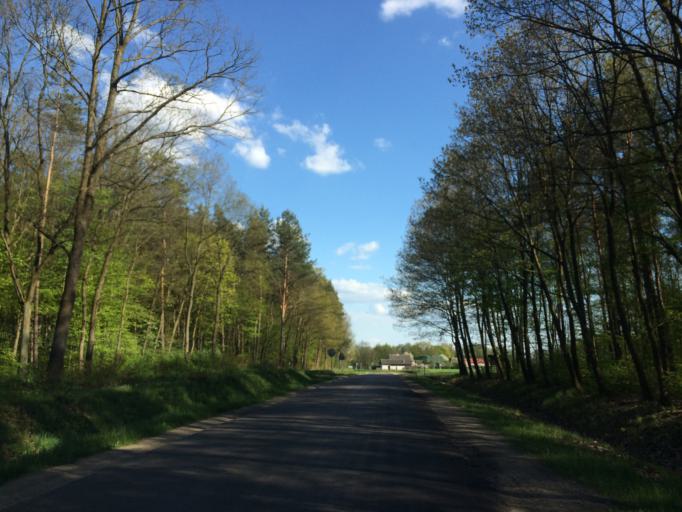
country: PL
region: Warmian-Masurian Voivodeship
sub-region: Powiat dzialdowski
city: Rybno
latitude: 53.3593
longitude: 19.9476
